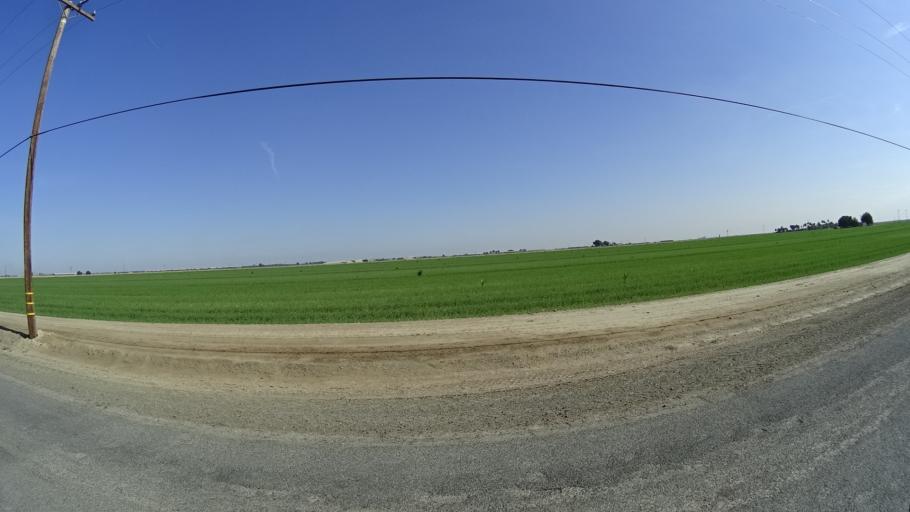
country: US
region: California
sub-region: Kings County
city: Home Garden
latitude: 36.2262
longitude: -119.5518
